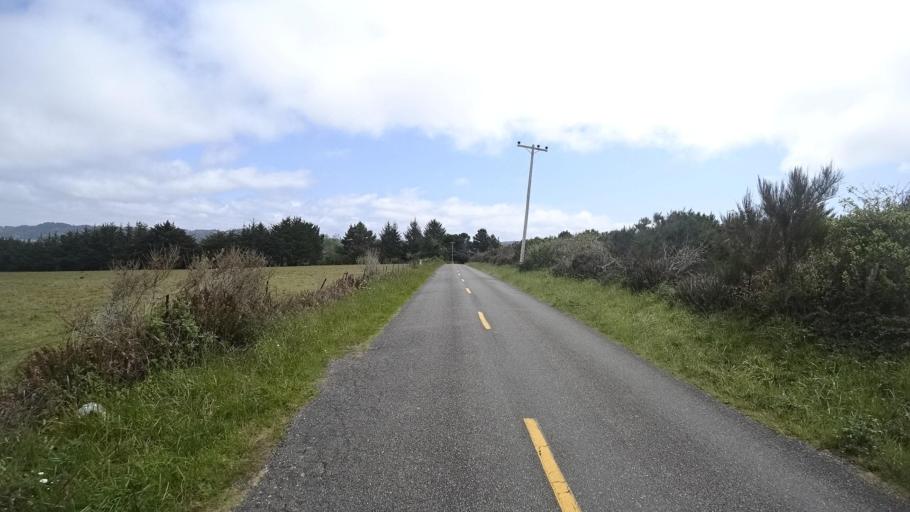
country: US
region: California
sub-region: Humboldt County
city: Humboldt Hill
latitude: 40.6869
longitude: -124.2420
